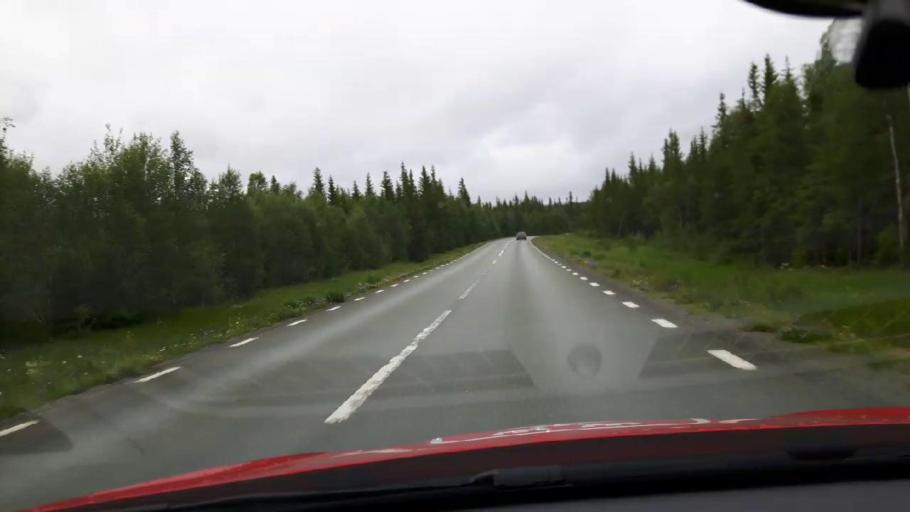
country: SE
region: Jaemtland
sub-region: Are Kommun
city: Are
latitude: 63.3023
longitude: 12.4223
